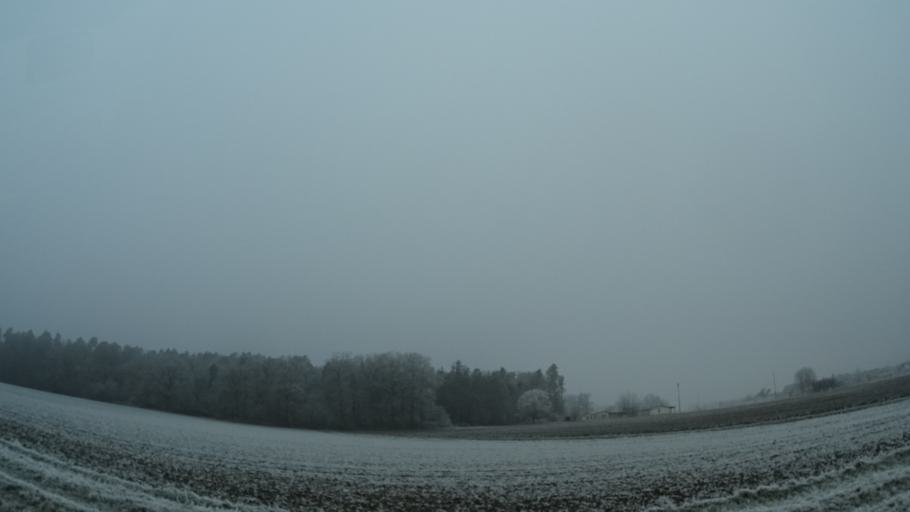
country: DE
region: Bavaria
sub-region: Regierungsbezirk Unterfranken
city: Frankenwinheim
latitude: 49.8592
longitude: 10.2950
